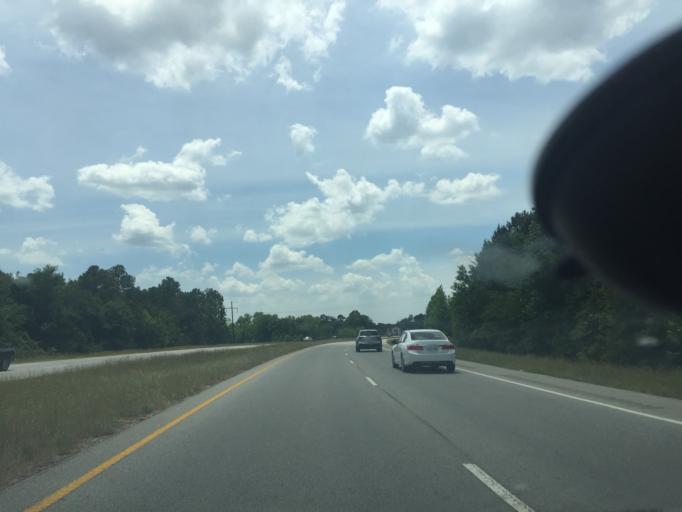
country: US
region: Georgia
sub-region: Bulloch County
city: Statesboro
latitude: 32.4116
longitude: -81.7572
